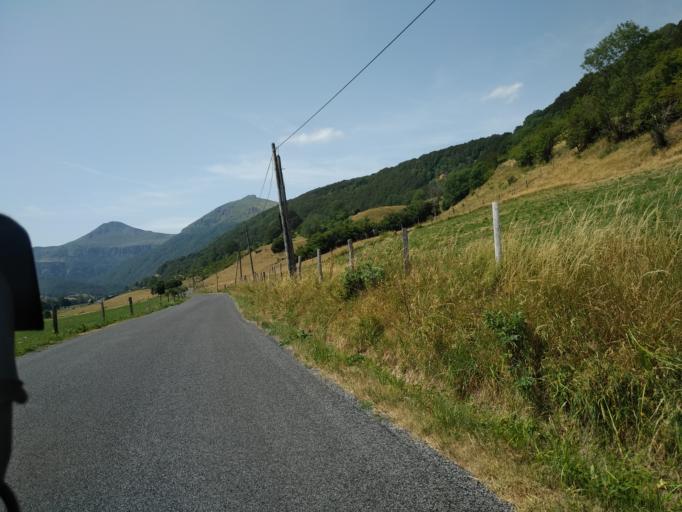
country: FR
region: Auvergne
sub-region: Departement du Cantal
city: Riom-es-Montagnes
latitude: 45.1534
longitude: 2.7021
